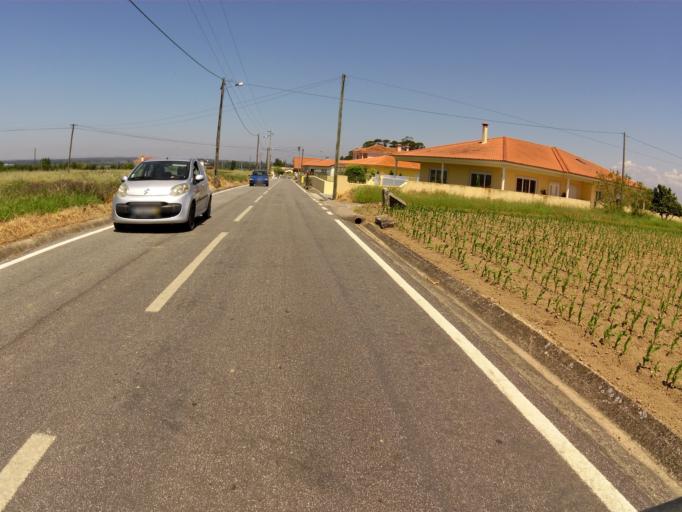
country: PT
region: Coimbra
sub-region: Montemor-O-Velho
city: Montemor-o-Velho
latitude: 40.1568
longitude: -8.7128
